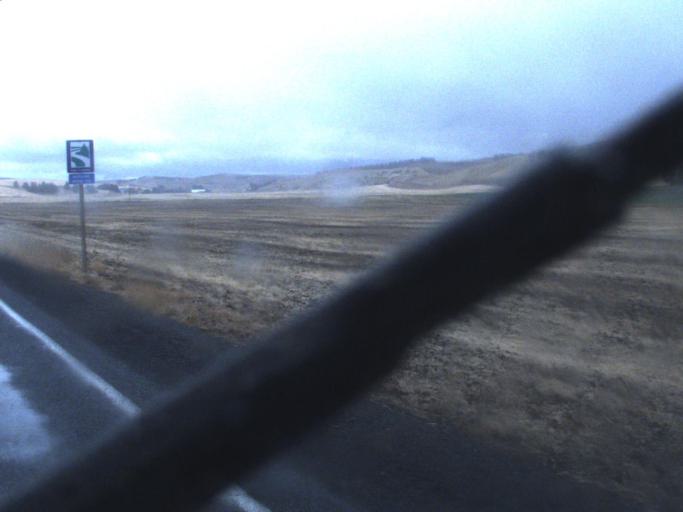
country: US
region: Washington
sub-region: Whitman County
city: Colfax
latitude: 47.0680
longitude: -117.5302
